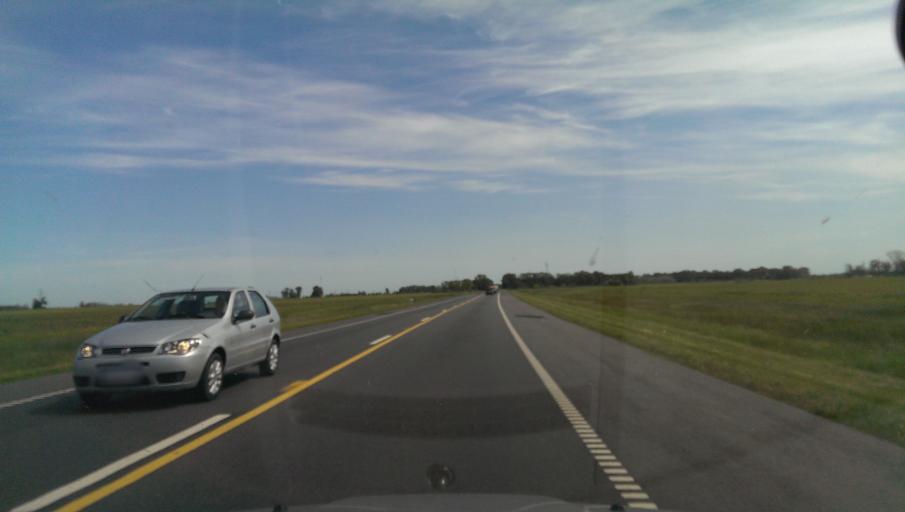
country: AR
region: Buenos Aires
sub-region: Partido de Las Flores
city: Las Flores
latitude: -36.3697
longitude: -59.4681
